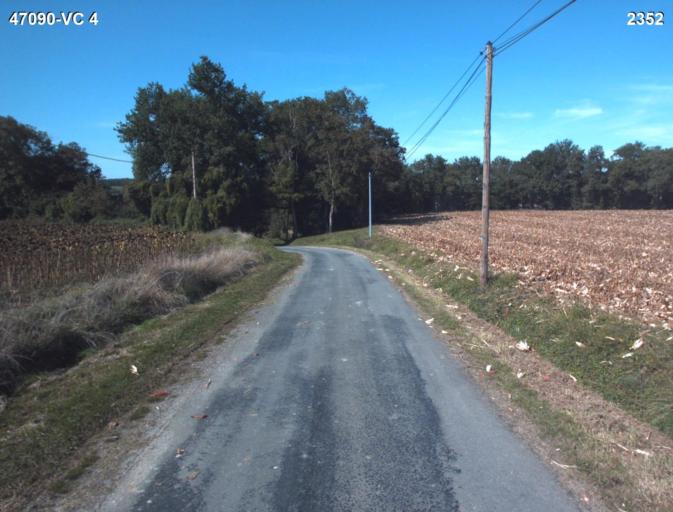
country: FR
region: Aquitaine
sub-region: Departement du Lot-et-Garonne
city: Nerac
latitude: 44.1744
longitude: 0.3676
